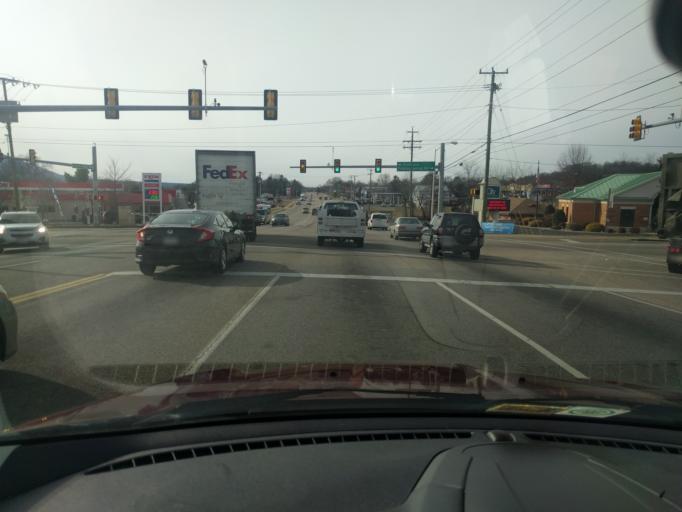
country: US
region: Virginia
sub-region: Augusta County
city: Stuarts Draft
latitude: 38.0348
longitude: -79.0345
